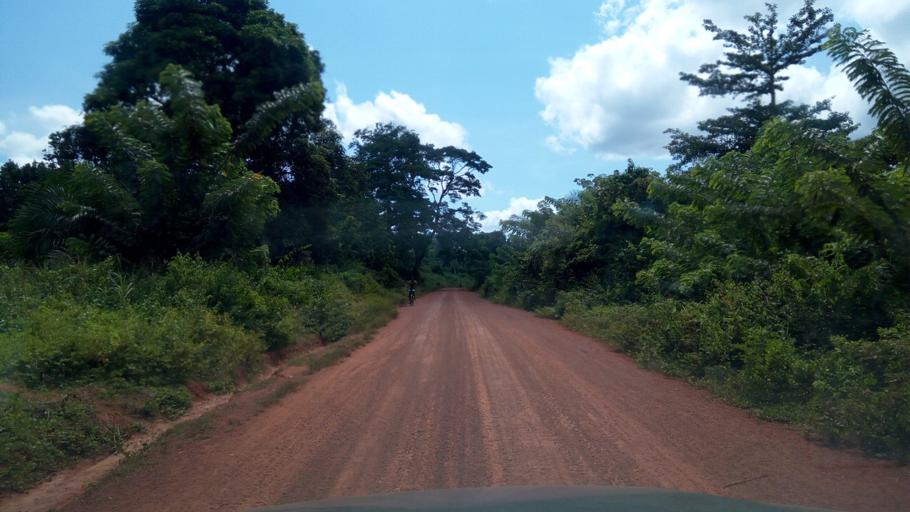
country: CF
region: Bangui
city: Bangui
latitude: 4.2165
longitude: 18.6921
